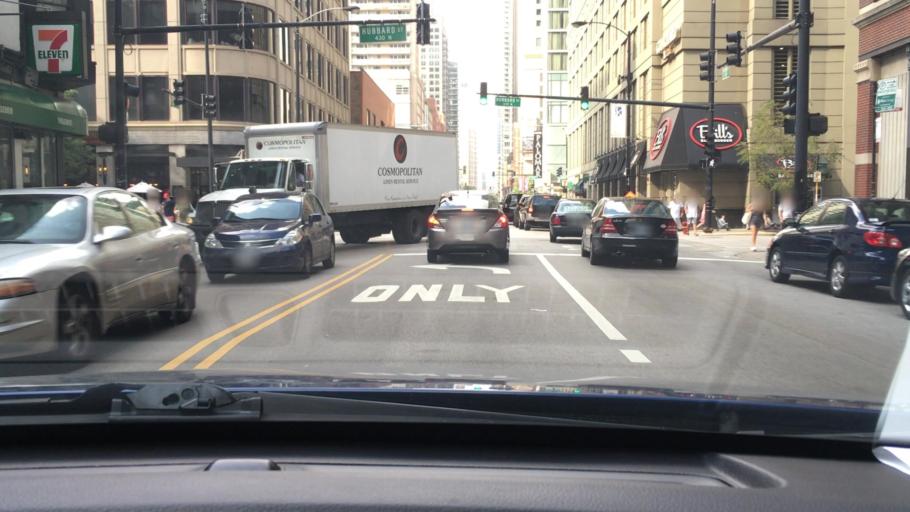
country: US
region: Illinois
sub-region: Cook County
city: Chicago
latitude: 41.8897
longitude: -87.6279
